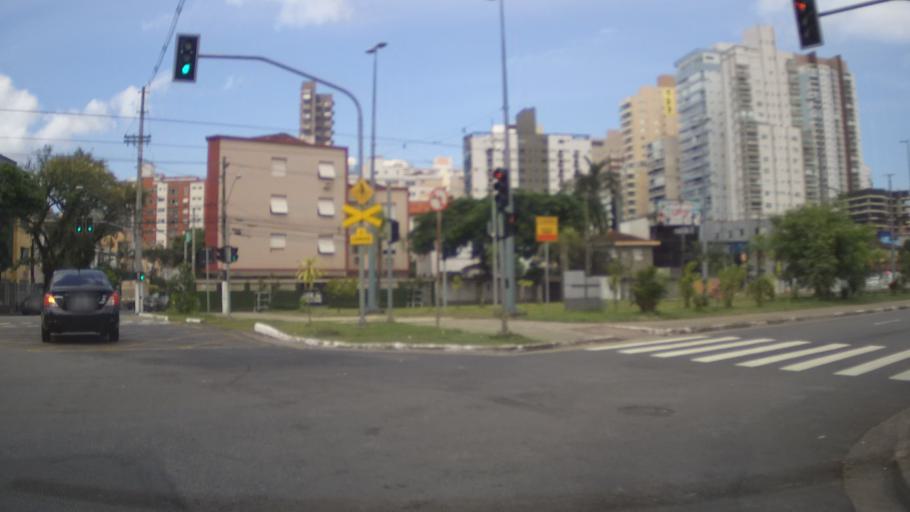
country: BR
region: Sao Paulo
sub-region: Santos
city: Santos
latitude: -23.9620
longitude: -46.3408
